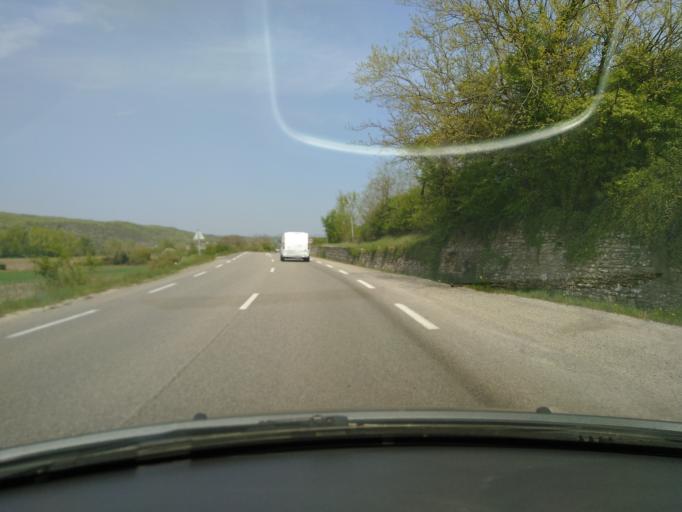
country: FR
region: Rhone-Alpes
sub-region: Departement de l'Ardeche
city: Saint-Sernin
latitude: 44.5184
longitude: 4.3975
